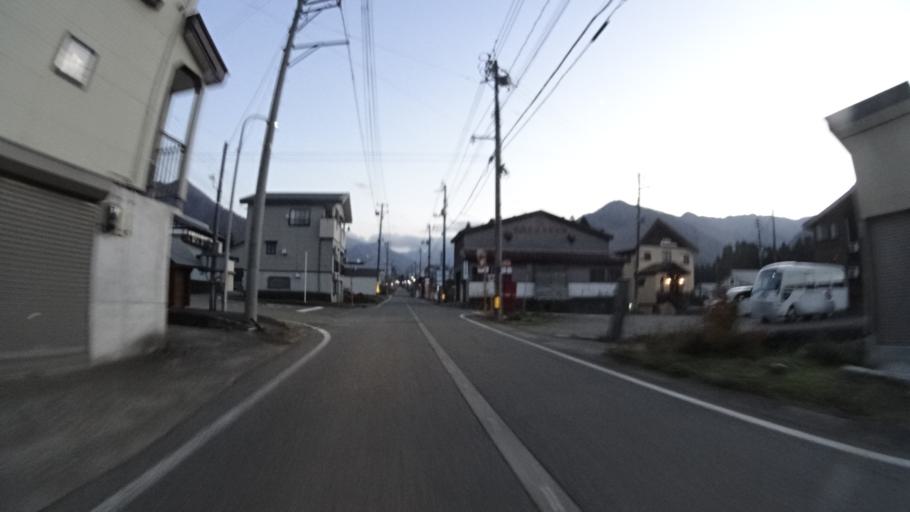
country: JP
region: Niigata
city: Shiozawa
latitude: 36.9137
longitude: 138.8460
